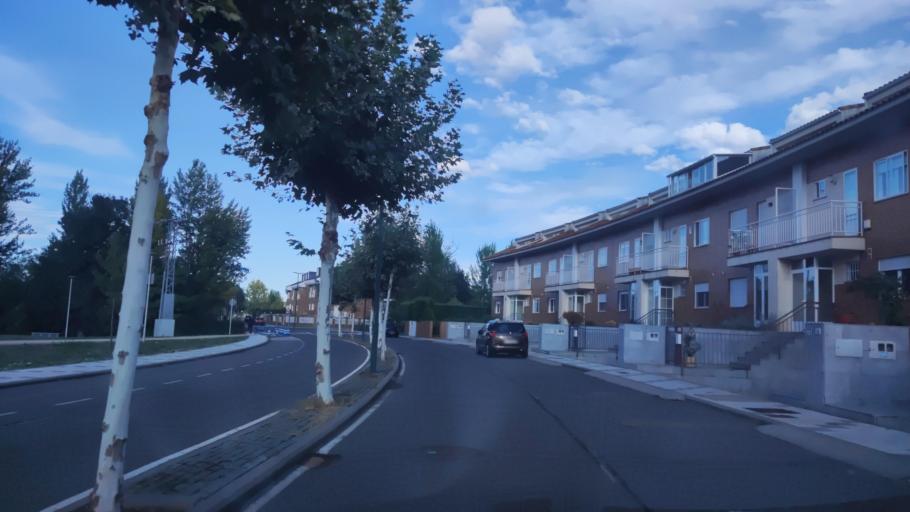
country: ES
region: Castille and Leon
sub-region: Provincia de Salamanca
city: Salamanca
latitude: 40.9548
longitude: -5.6517
